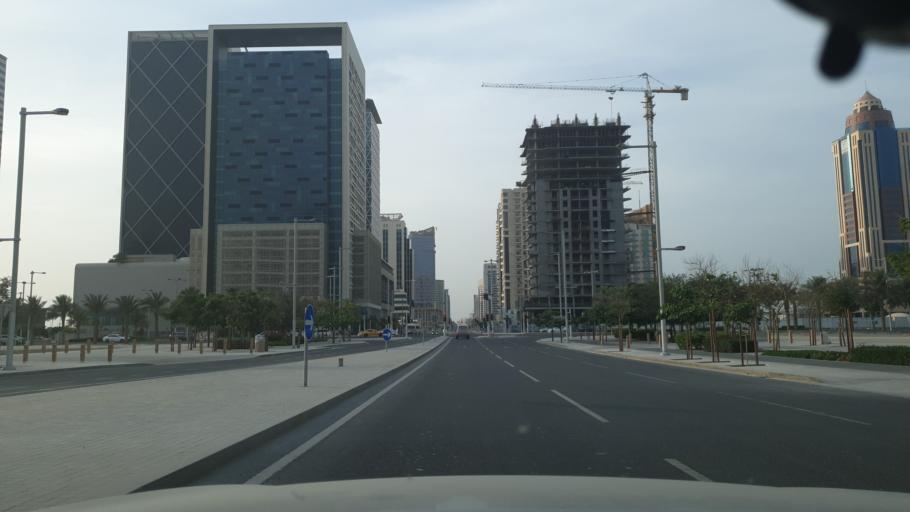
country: QA
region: Baladiyat ad Dawhah
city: Doha
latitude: 25.3820
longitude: 51.5264
